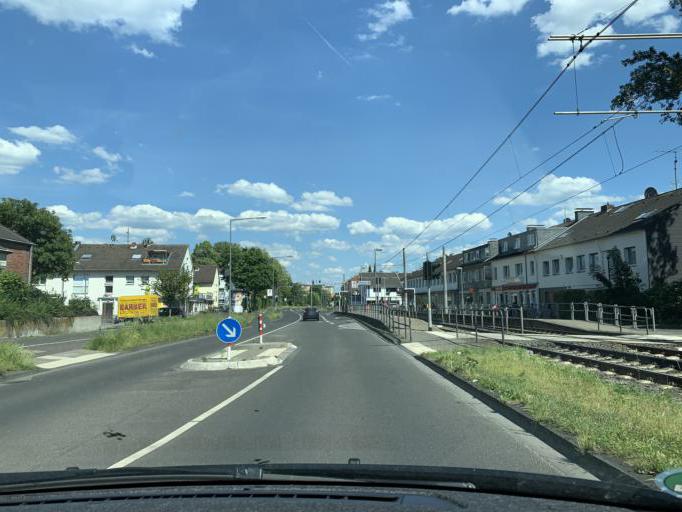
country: DE
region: North Rhine-Westphalia
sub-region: Regierungsbezirk Koln
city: Bilderstoeckchen
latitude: 50.9948
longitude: 6.9245
